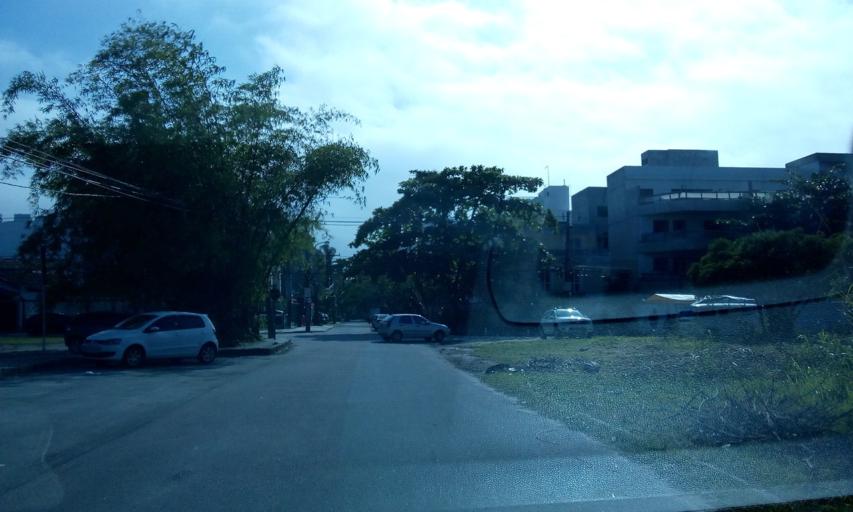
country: BR
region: Rio de Janeiro
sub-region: Nilopolis
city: Nilopolis
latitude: -23.0110
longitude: -43.4460
